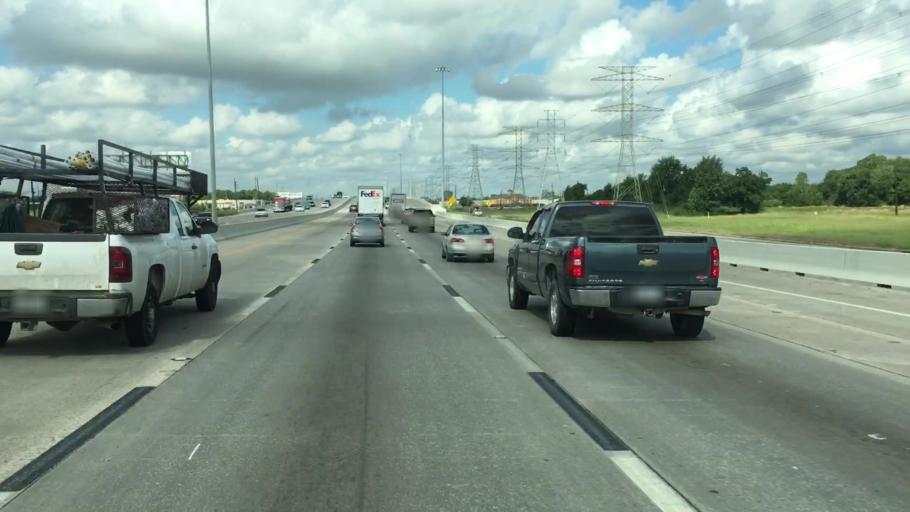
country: US
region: Texas
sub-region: Harris County
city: Aldine
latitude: 29.9442
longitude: -95.3496
